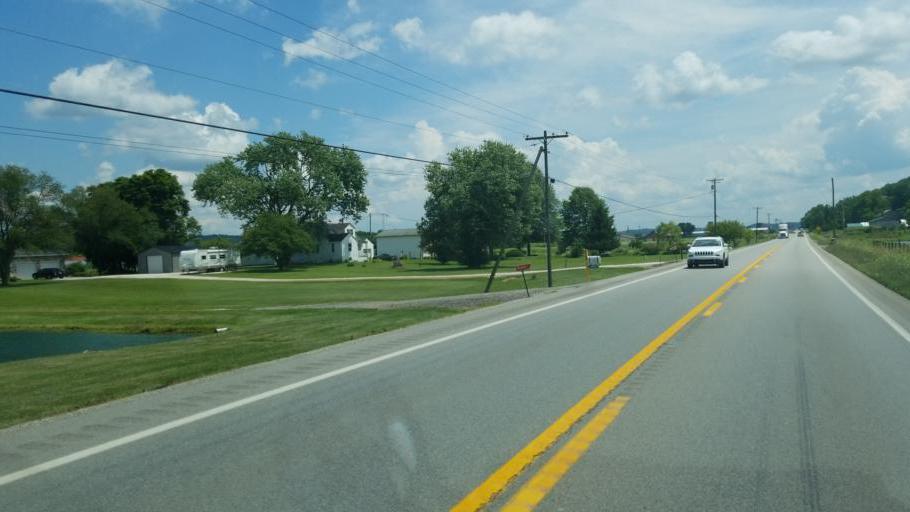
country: US
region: West Virginia
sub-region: Putnam County
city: Buffalo
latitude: 38.7636
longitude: -82.0008
